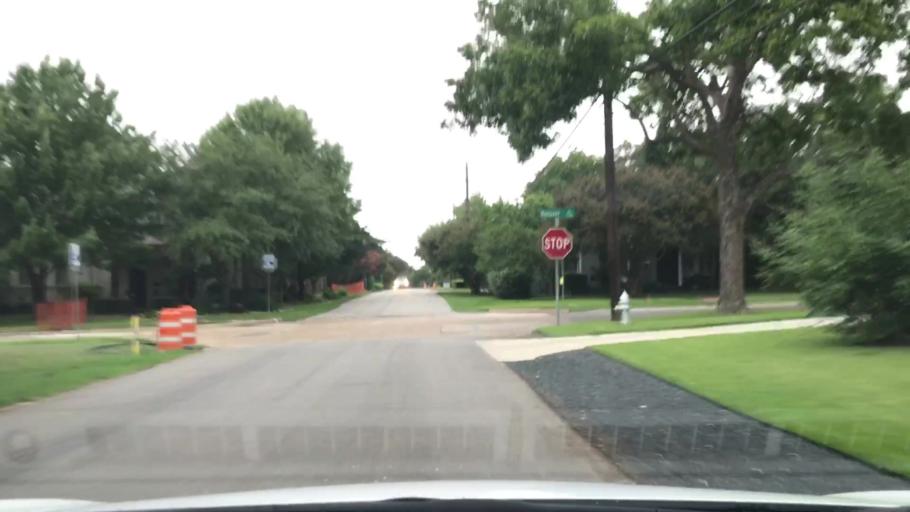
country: US
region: Texas
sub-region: Dallas County
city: University Park
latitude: 32.8549
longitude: -96.8252
